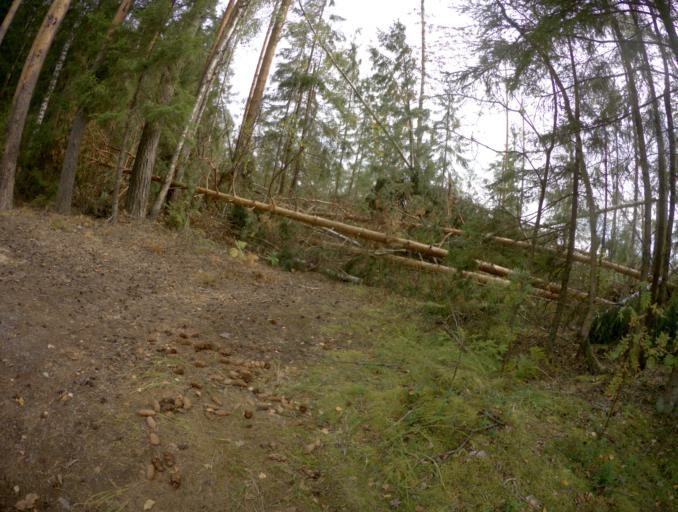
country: RU
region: Vladimir
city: Ivanishchi
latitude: 55.8602
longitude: 40.3725
